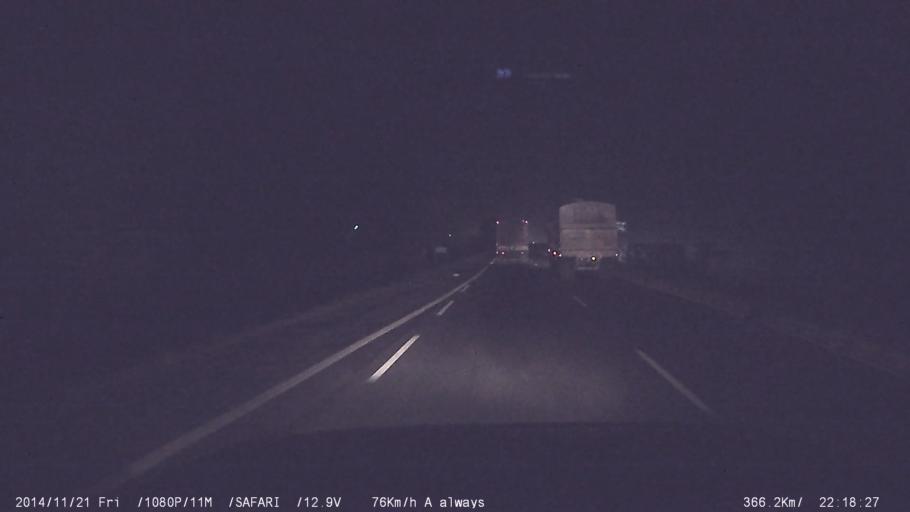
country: IN
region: Tamil Nadu
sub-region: Kancheepuram
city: Madurantakam
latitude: 12.3928
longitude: 79.8036
